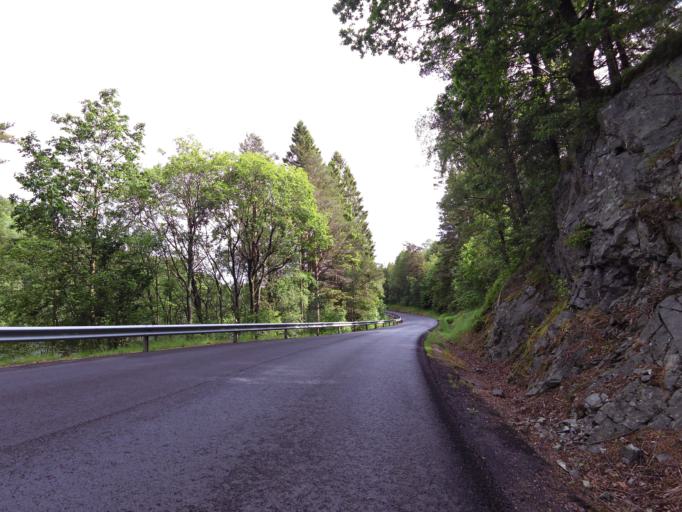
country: NO
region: Vest-Agder
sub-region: Lindesnes
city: Vigeland
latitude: 58.0578
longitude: 7.2189
